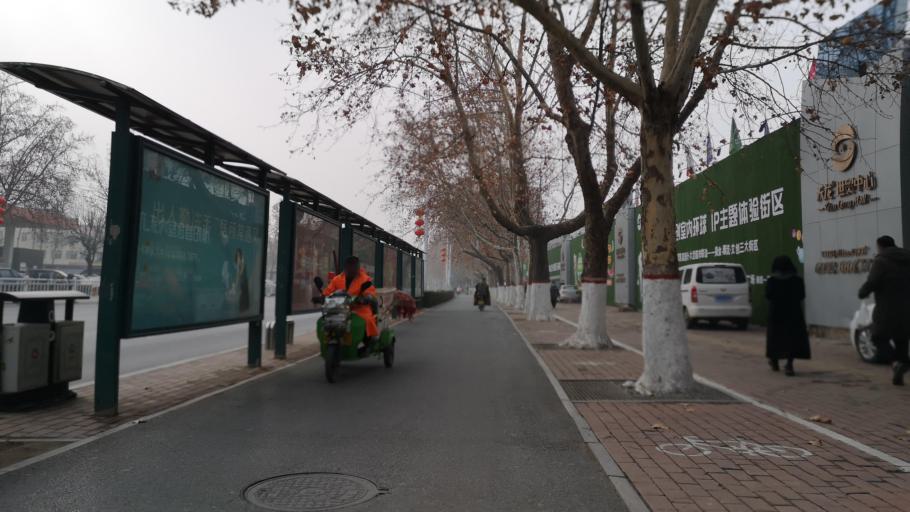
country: CN
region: Henan Sheng
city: Zhongyuanlu
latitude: 35.7753
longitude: 115.0405
